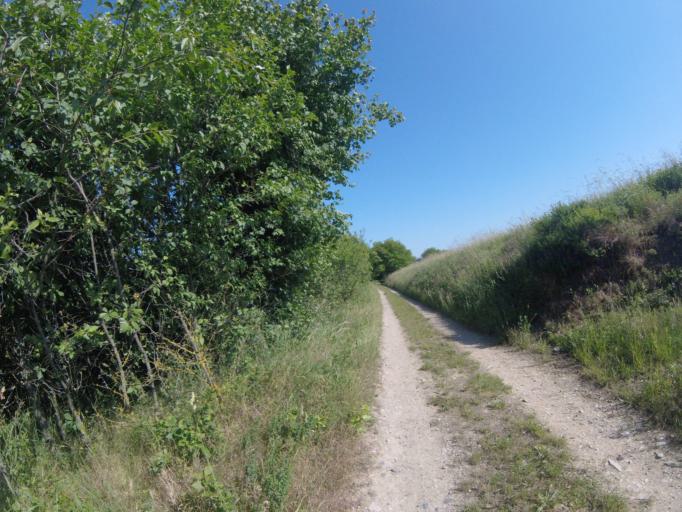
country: HU
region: Zala
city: Zalaszentgrot
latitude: 46.8964
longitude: 17.0682
